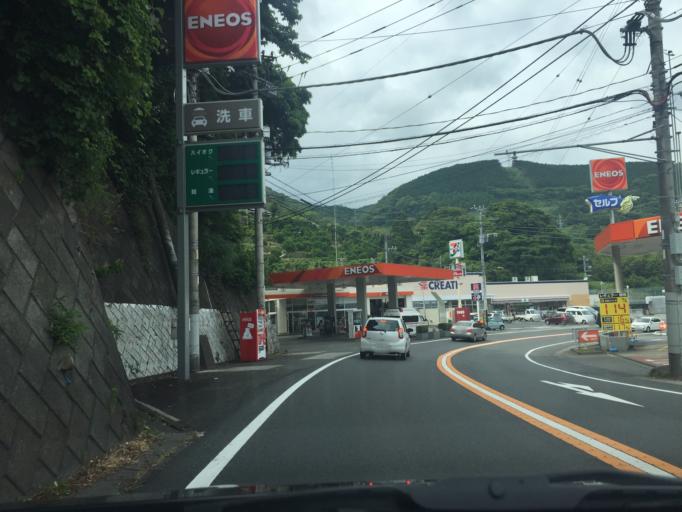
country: JP
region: Shizuoka
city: Shimoda
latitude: 34.7750
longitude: 139.0349
